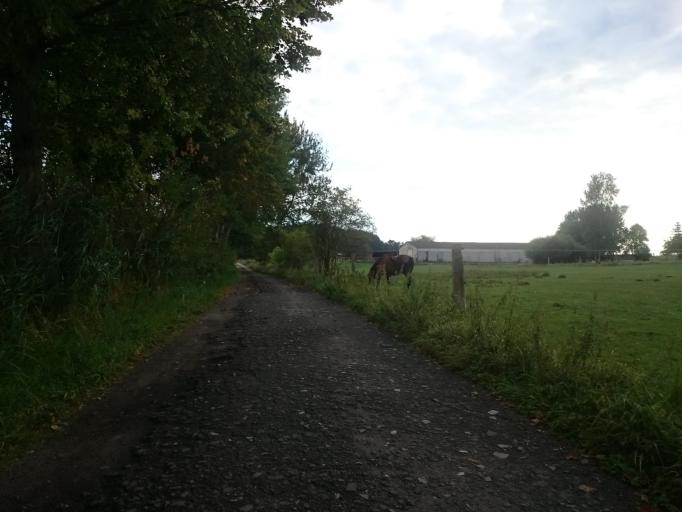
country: DE
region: Mecklenburg-Vorpommern
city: Neustrelitz
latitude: 53.2946
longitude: 13.0742
